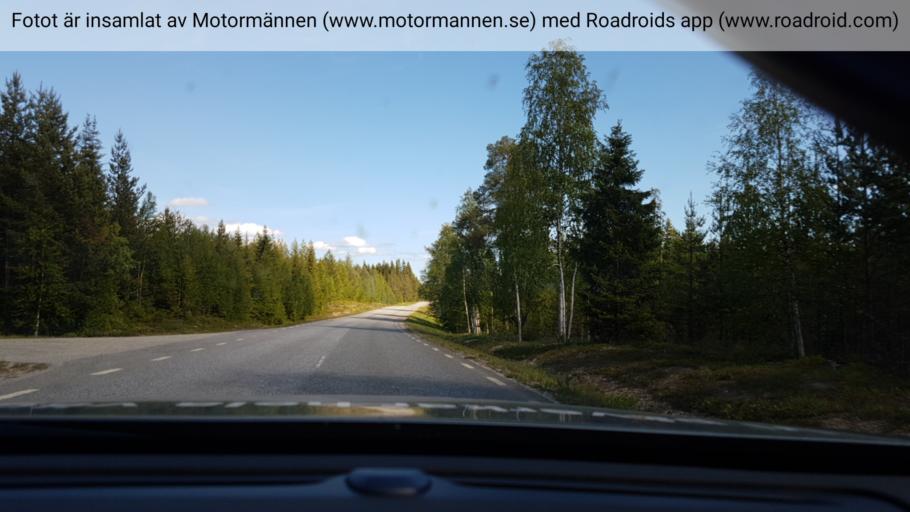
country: SE
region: Vaesterbotten
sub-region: Lycksele Kommun
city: Soderfors
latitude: 64.6229
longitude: 18.1215
